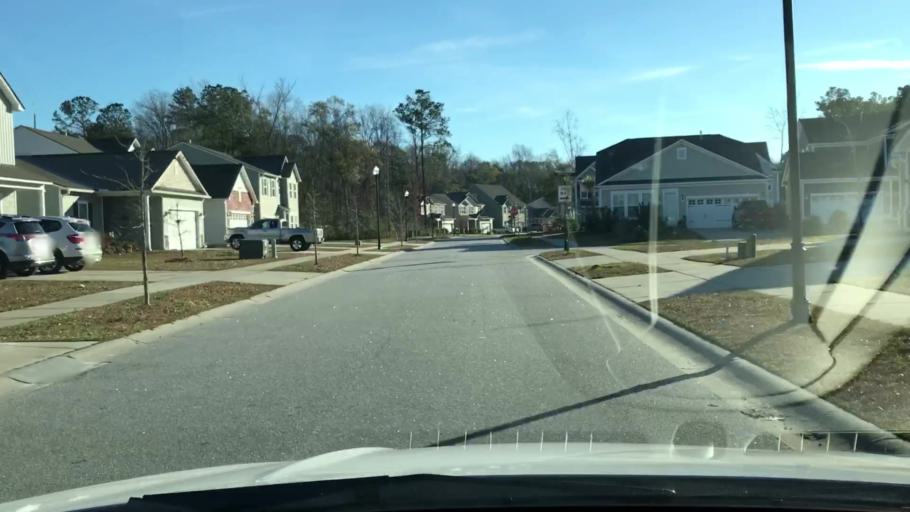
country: US
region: South Carolina
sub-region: Charleston County
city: Shell Point
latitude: 32.8132
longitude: -80.0734
